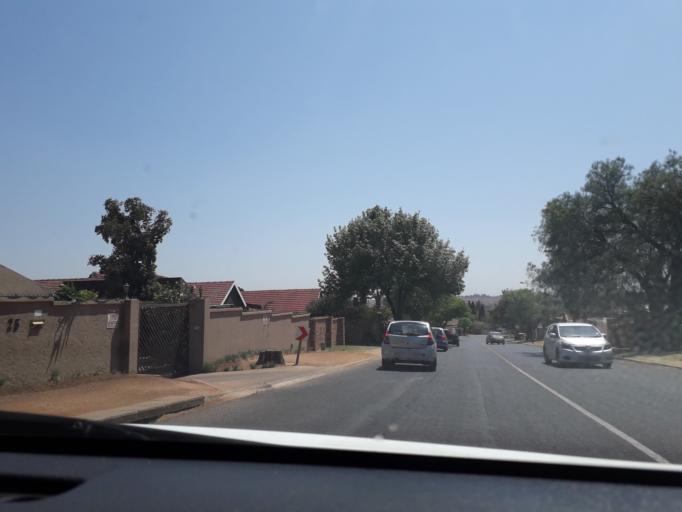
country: ZA
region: Gauteng
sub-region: Ekurhuleni Metropolitan Municipality
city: Tembisa
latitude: -26.0589
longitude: 28.2208
